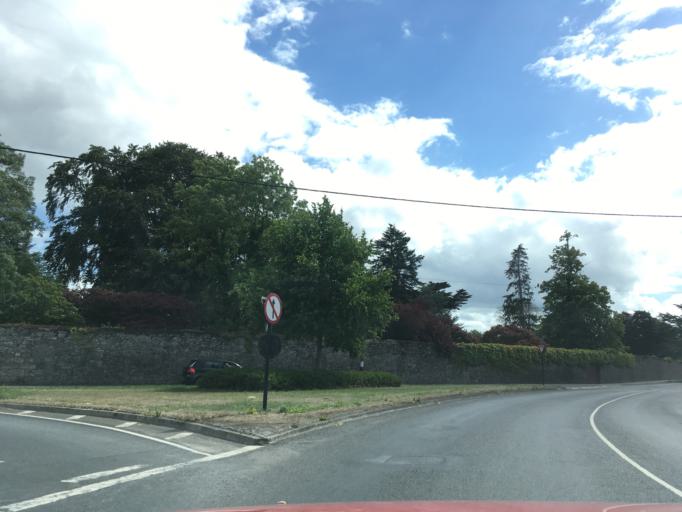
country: IE
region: Munster
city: Cahir
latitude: 52.3741
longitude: -7.9312
